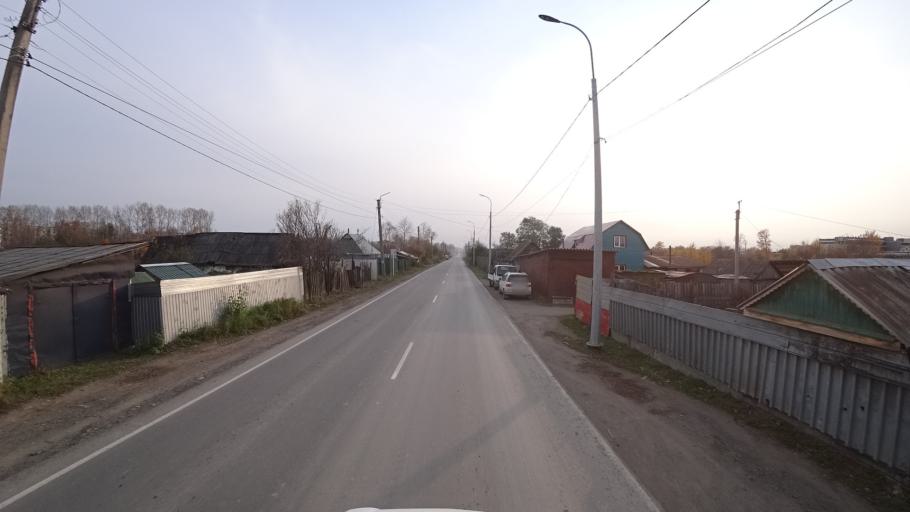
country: RU
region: Khabarovsk Krai
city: Amursk
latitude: 50.1043
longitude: 136.5124
